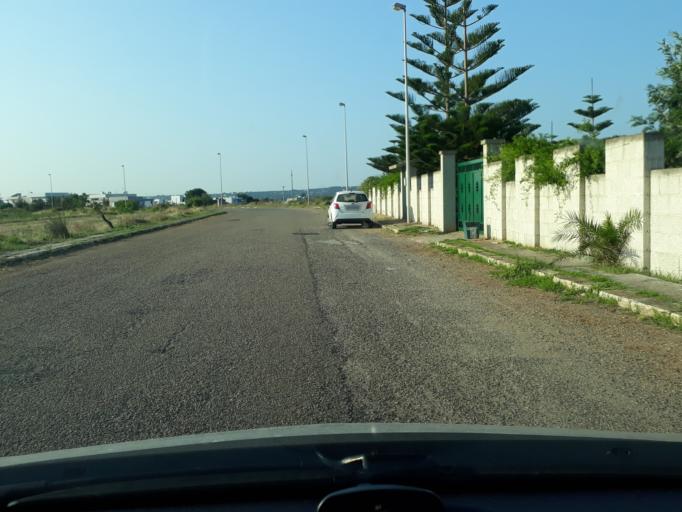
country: IT
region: Apulia
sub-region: Provincia di Brindisi
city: Carovigno
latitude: 40.7598
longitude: 17.6905
